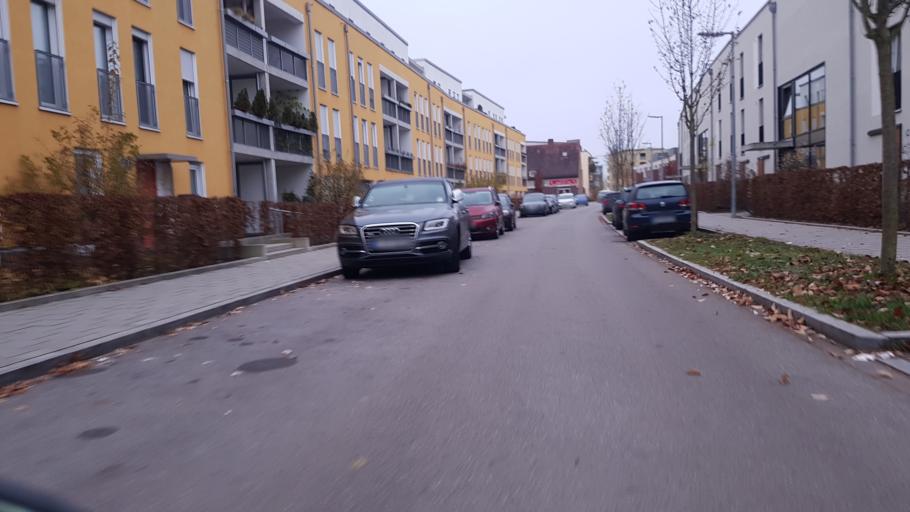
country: DE
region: Bavaria
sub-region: Upper Bavaria
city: Bogenhausen
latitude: 48.1224
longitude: 11.6257
